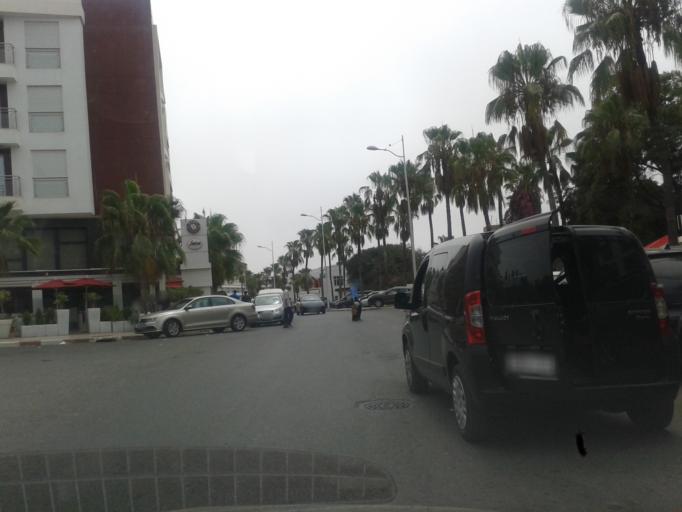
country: MA
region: Souss-Massa-Draa
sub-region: Agadir-Ida-ou-Tnan
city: Agadir
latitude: 30.4236
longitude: -9.6052
